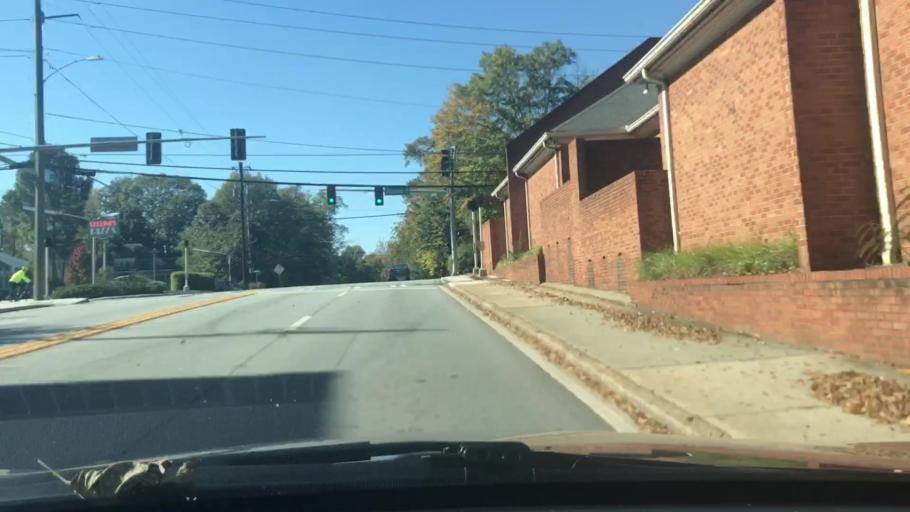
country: US
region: Georgia
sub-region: DeKalb County
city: Decatur
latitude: 33.7736
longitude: -84.2892
